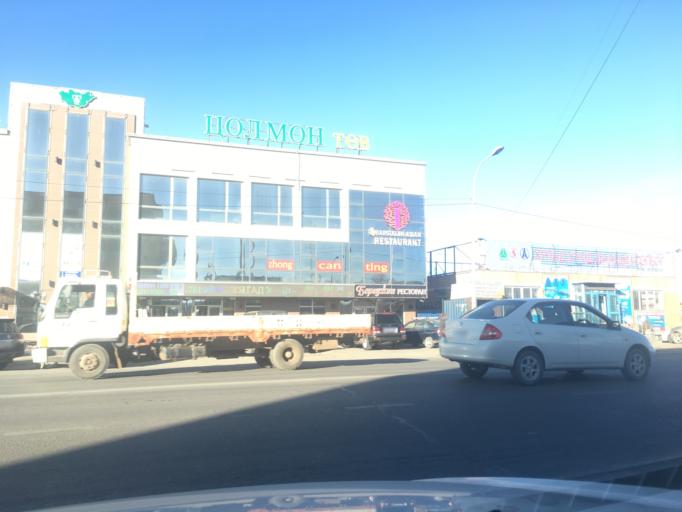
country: MN
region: Ulaanbaatar
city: Ulaanbaatar
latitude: 47.9083
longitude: 106.7985
